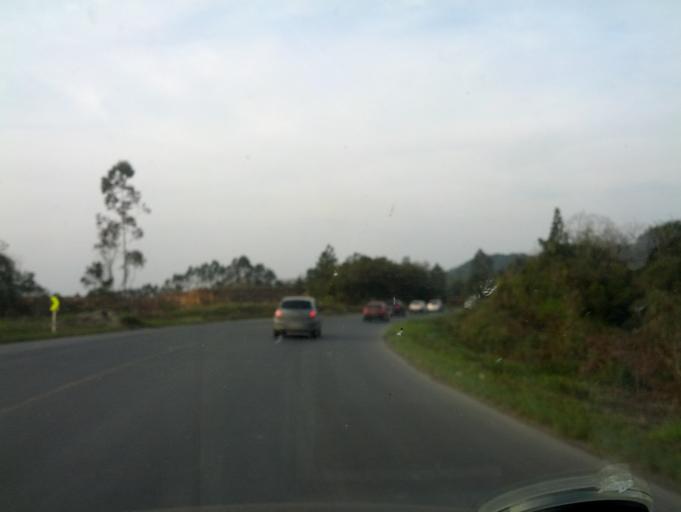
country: BR
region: Santa Catarina
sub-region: Otacilio Costa
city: Otacilio Costa
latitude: -27.2840
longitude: -50.0775
